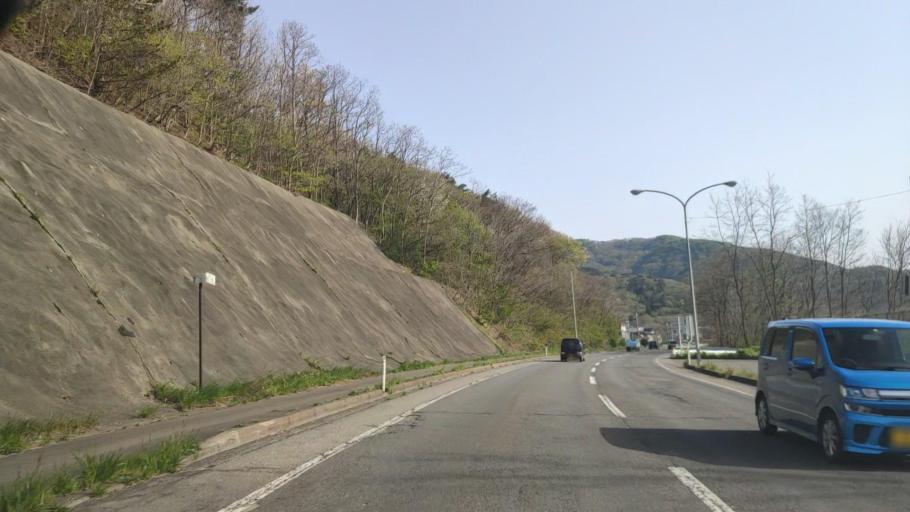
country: JP
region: Aomori
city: Aomori Shi
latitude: 40.8748
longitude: 140.8516
